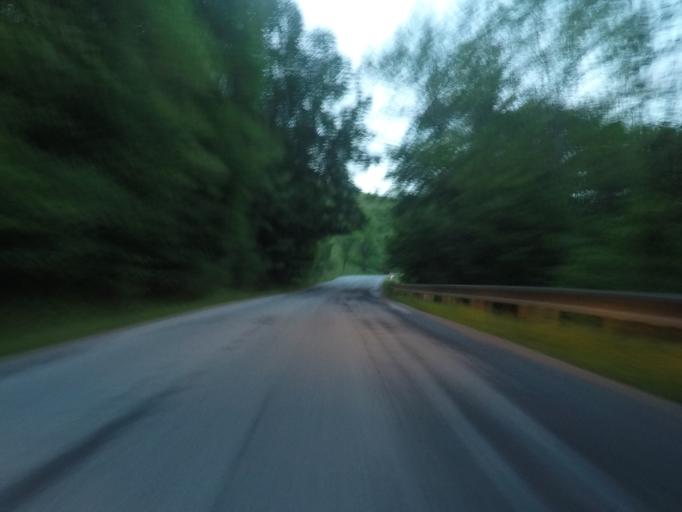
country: SK
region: Banskobystricky
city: Tisovec
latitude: 48.6906
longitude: 19.9682
